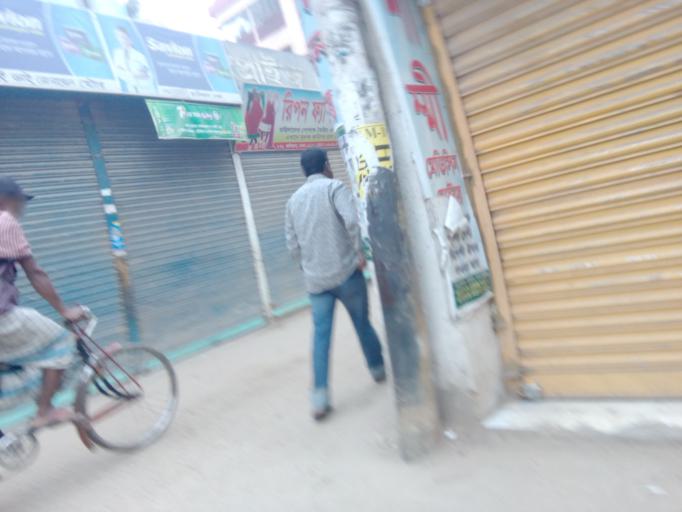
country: BD
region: Dhaka
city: Paltan
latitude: 23.7462
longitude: 90.4167
